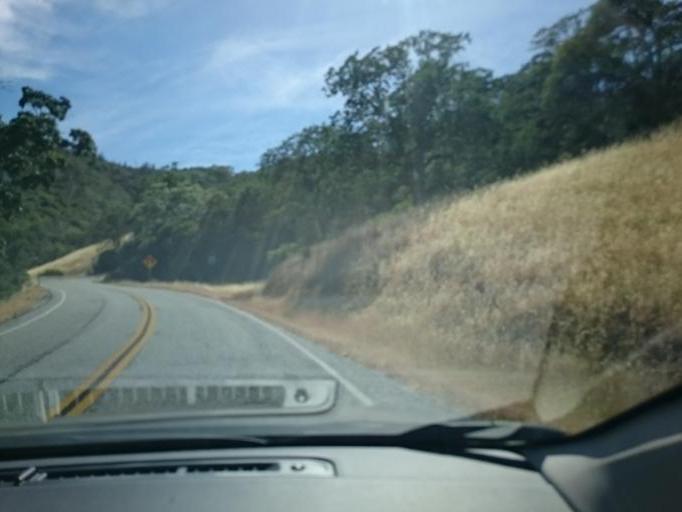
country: US
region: California
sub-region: Santa Clara County
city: East Foothills
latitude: 37.3489
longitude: -121.5983
